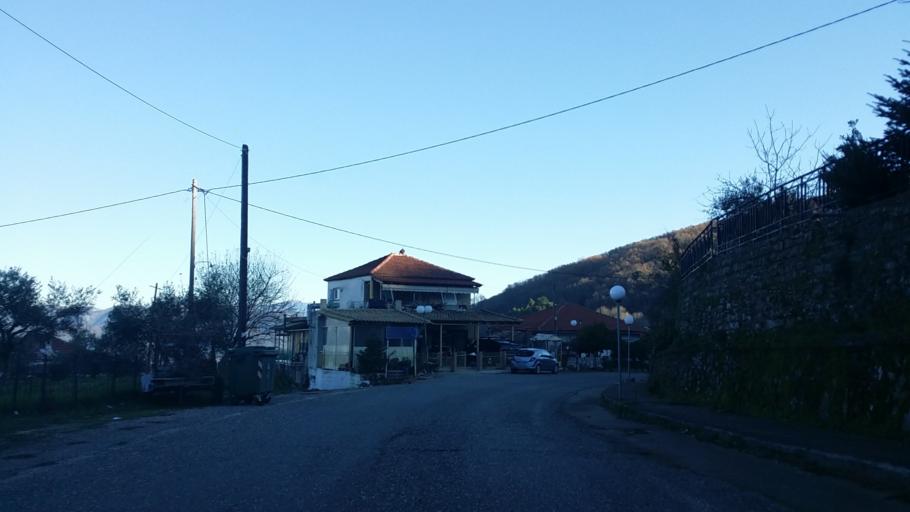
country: GR
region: West Greece
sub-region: Nomos Aitolias kai Akarnanias
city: Sardinia
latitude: 38.8684
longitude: 21.2870
